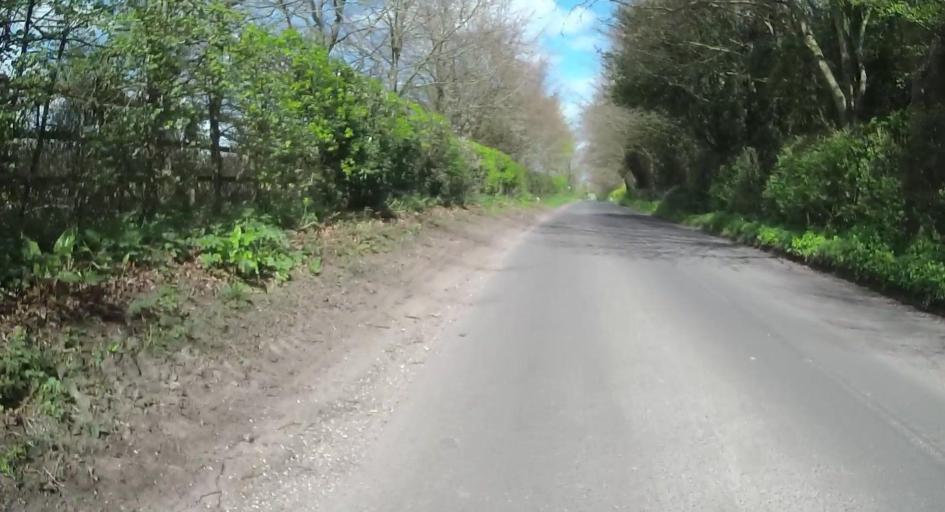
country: GB
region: England
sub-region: Hampshire
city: Abbotts Ann
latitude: 51.1014
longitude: -1.5087
